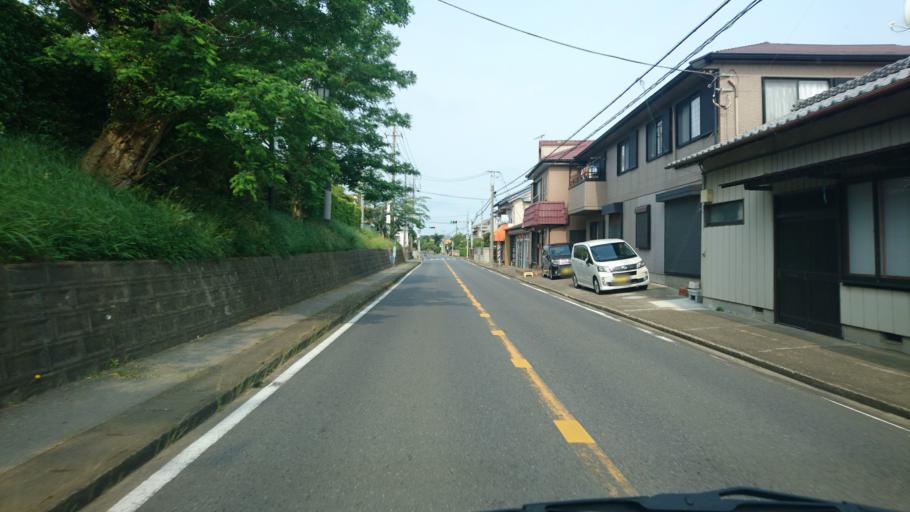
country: JP
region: Ibaraki
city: Edosaki
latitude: 35.8814
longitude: 140.3620
